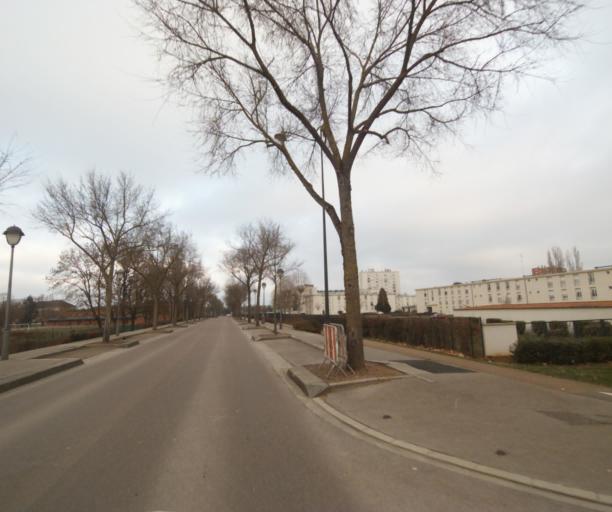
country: FR
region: Champagne-Ardenne
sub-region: Departement de la Haute-Marne
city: Bettancourt-la-Ferree
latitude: 48.6415
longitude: 4.9681
